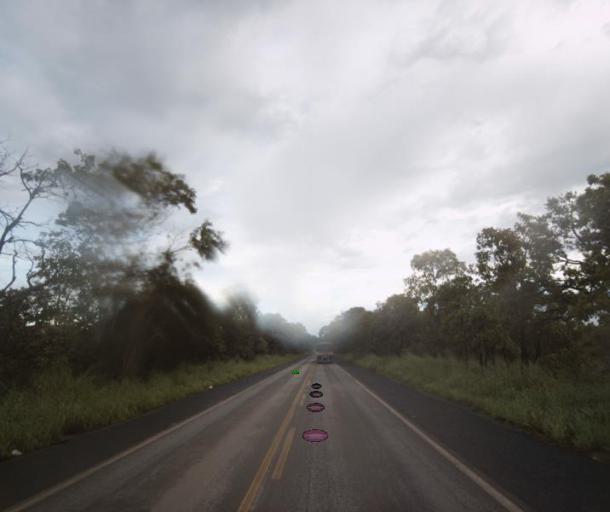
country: BR
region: Goias
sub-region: Porangatu
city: Porangatu
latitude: -13.9045
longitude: -49.0622
